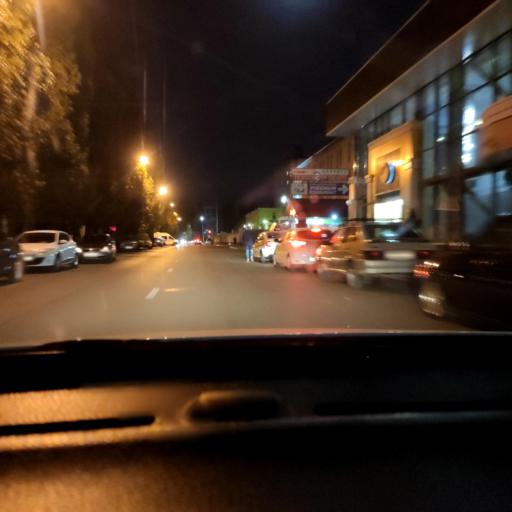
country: RU
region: Voronezj
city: Voronezh
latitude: 51.6805
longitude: 39.2568
